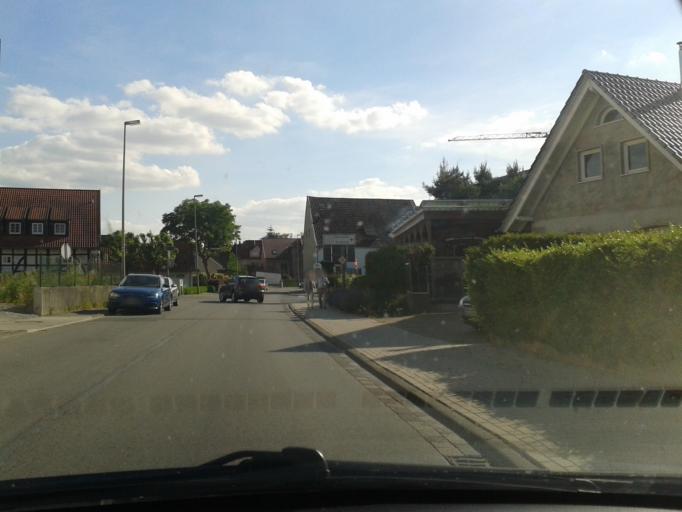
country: DE
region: North Rhine-Westphalia
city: Bad Lippspringe
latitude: 51.7800
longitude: 8.8256
